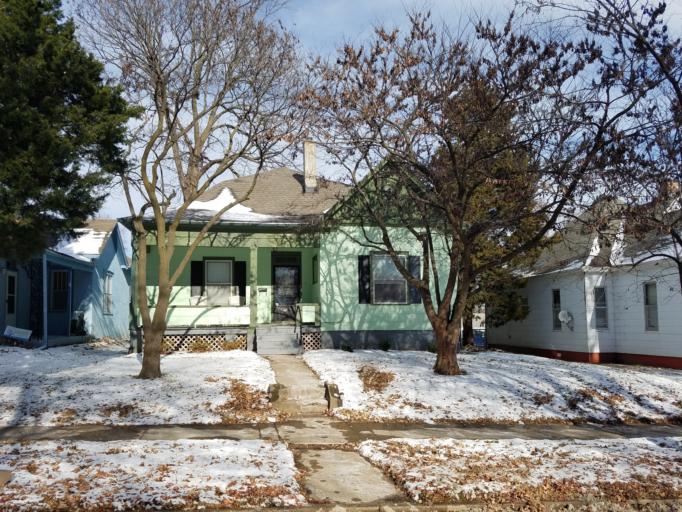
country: US
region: Missouri
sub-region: Lafayette County
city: Lexington
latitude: 39.1832
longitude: -93.8710
